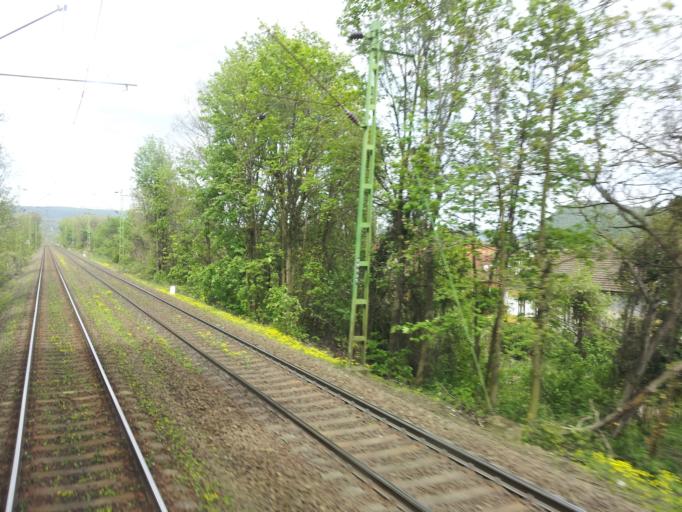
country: HU
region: Pest
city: Nagymaros
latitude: 47.7933
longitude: 18.9602
